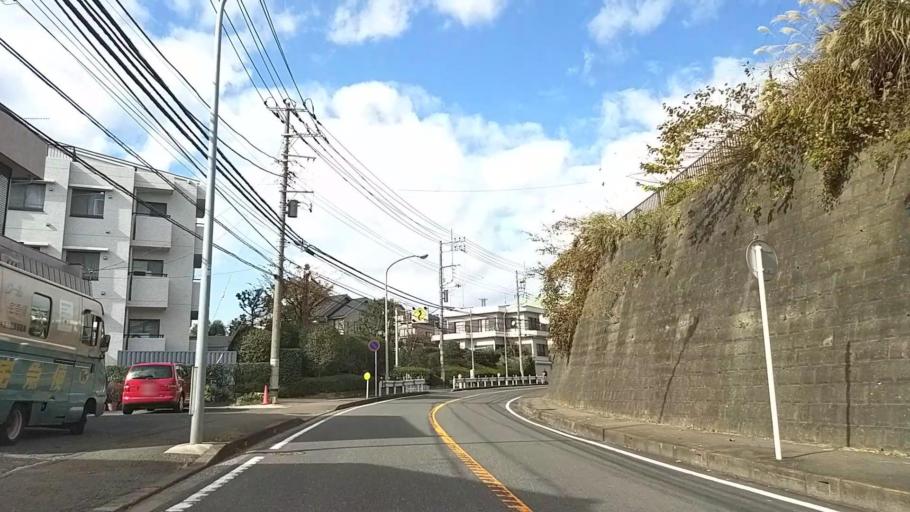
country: JP
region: Kanagawa
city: Yokohama
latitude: 35.4924
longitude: 139.6359
